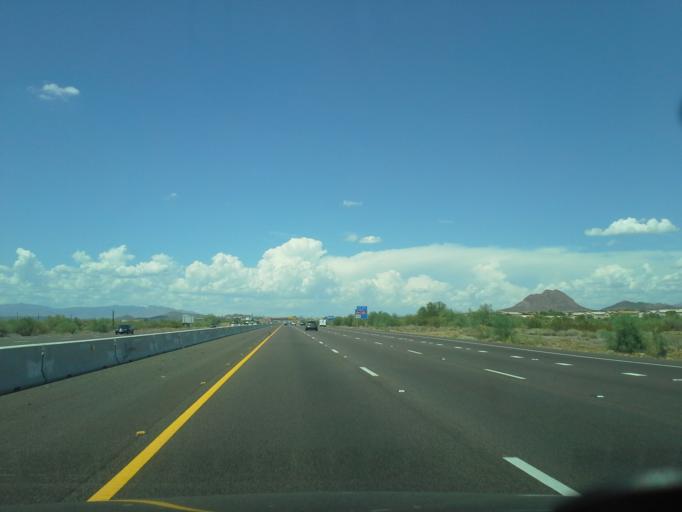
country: US
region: Arizona
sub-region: Maricopa County
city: Anthem
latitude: 33.8529
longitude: -112.1440
